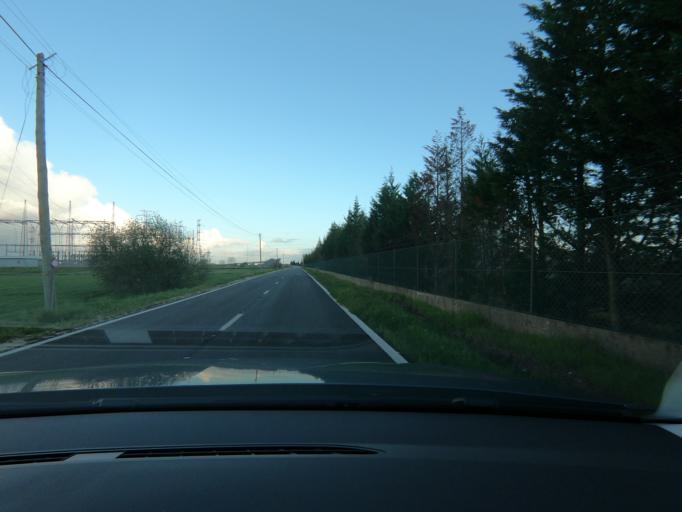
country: PT
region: Lisbon
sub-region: Alenquer
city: Carregado
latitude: 39.0145
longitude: -8.9543
